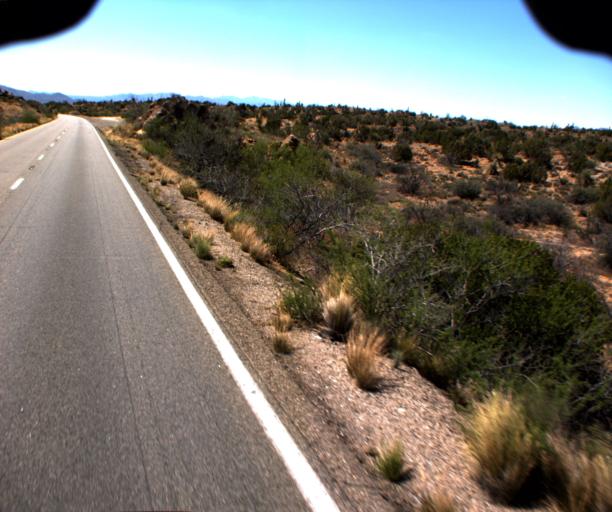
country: US
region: Arizona
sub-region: Yavapai County
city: Bagdad
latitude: 34.4819
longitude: -113.3458
